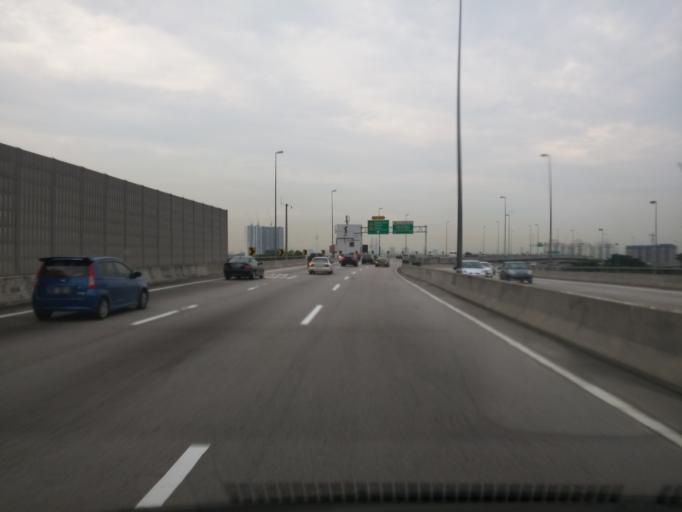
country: MY
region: Kuala Lumpur
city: Kuala Lumpur
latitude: 3.0866
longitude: 101.6940
